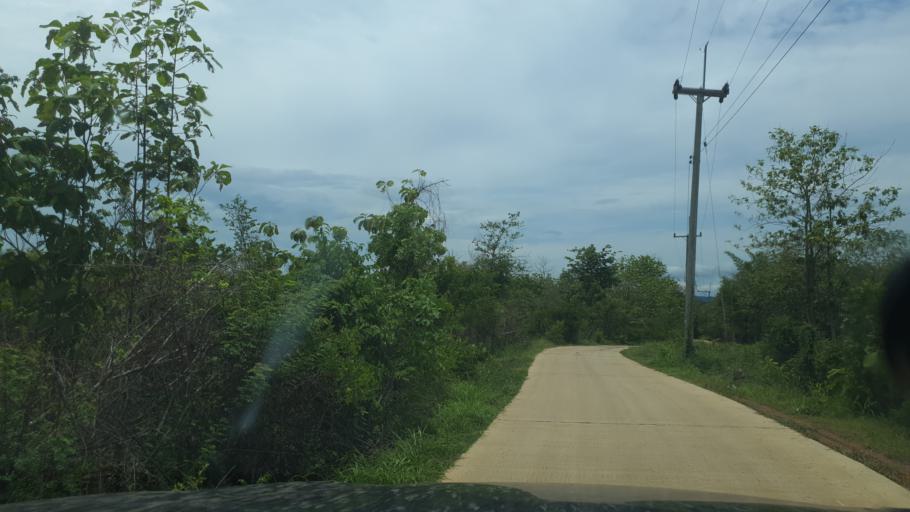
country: TH
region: Lampang
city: Ko Kha
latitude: 18.1333
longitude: 99.3323
